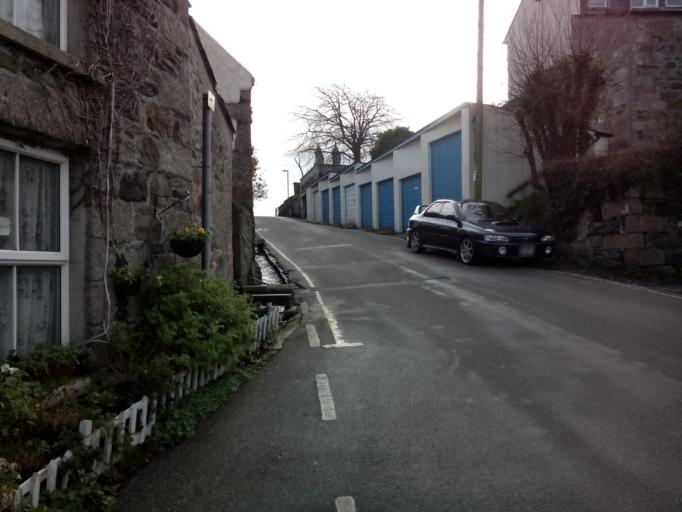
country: GB
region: England
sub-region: Cornwall
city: Helston
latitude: 50.1011
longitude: -5.2780
